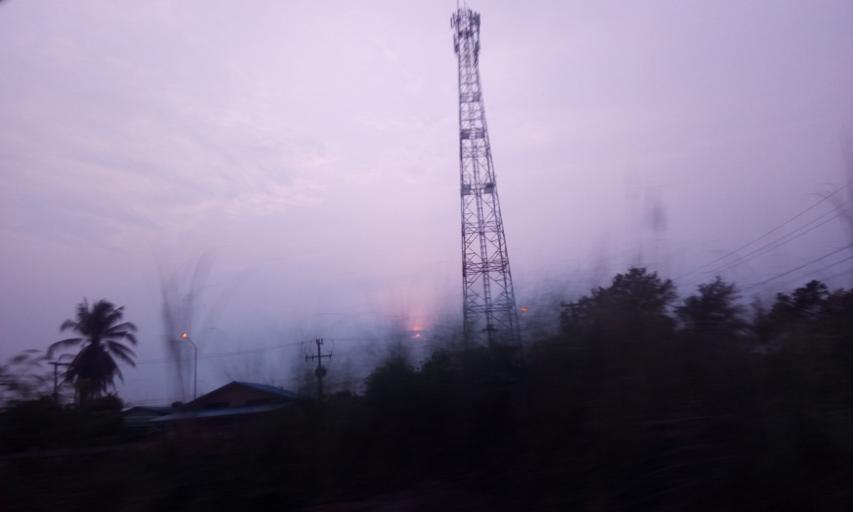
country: TH
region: Pathum Thani
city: Ban Lam Luk Ka
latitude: 14.0240
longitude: 100.8941
